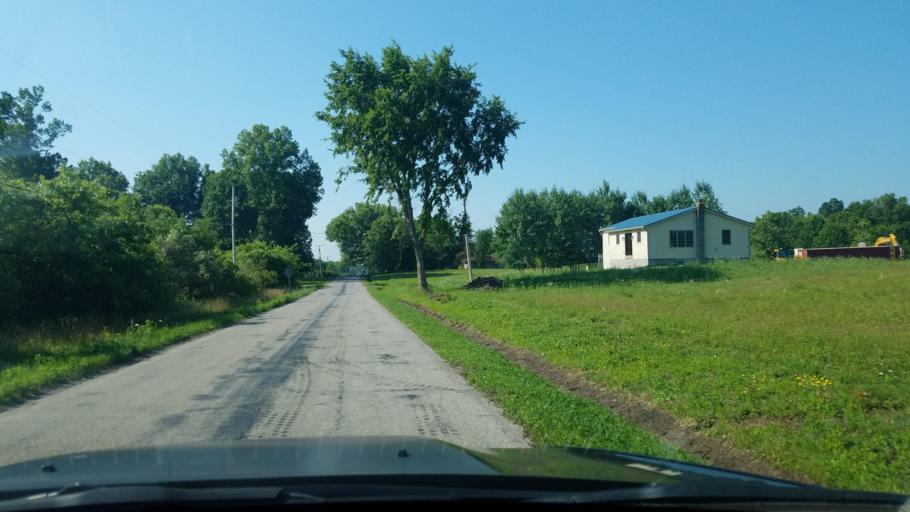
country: US
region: Ohio
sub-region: Trumbull County
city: Leavittsburg
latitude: 41.2890
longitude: -80.9059
